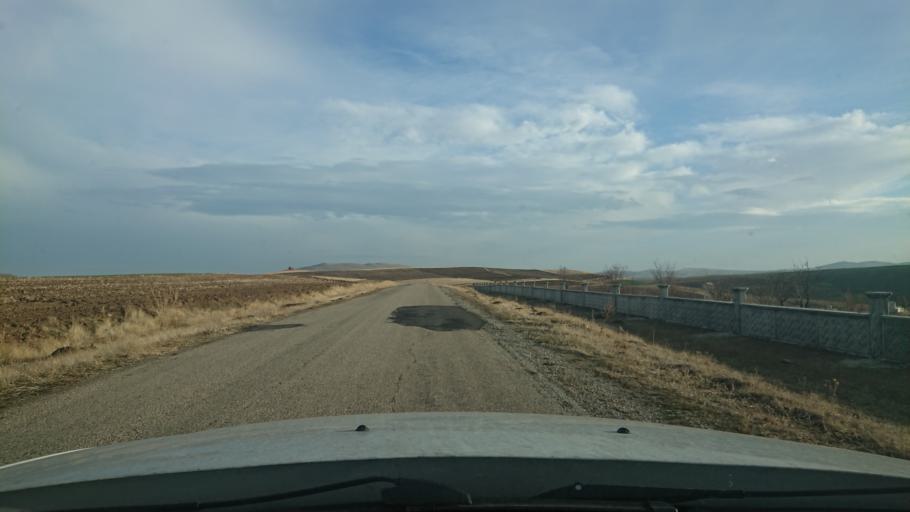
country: TR
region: Aksaray
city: Acipinar
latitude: 38.6628
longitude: 33.8448
